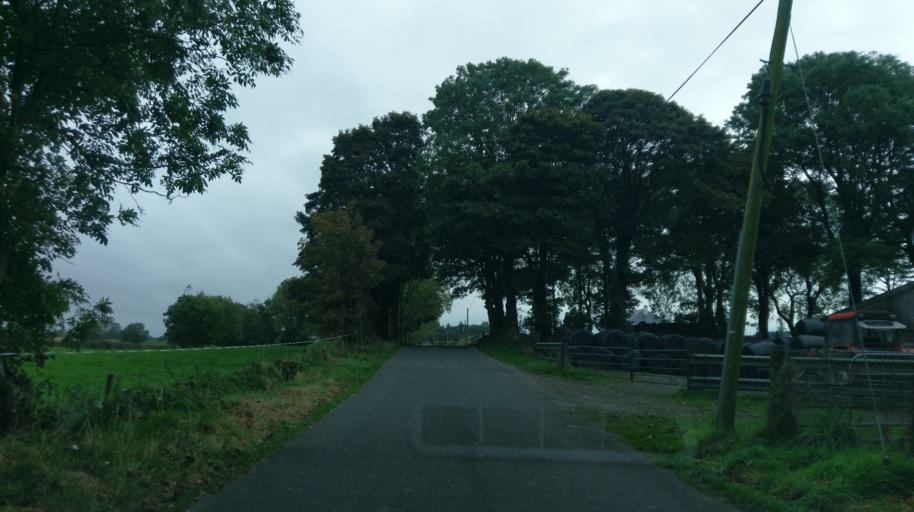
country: IE
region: Connaught
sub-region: County Galway
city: Athenry
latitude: 53.4575
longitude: -8.6106
